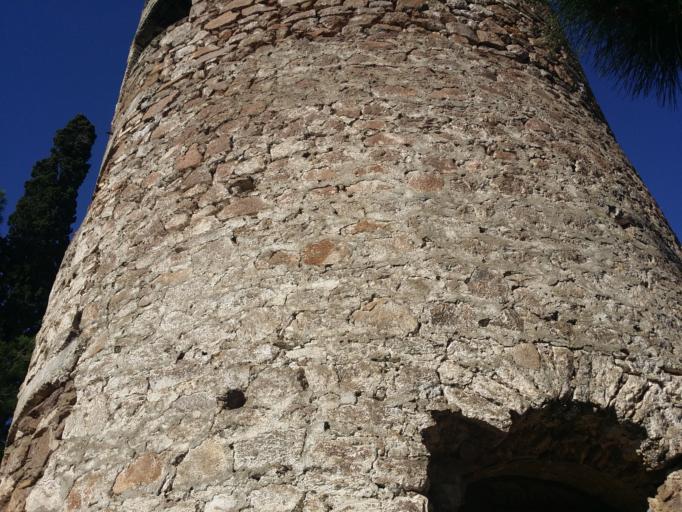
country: GR
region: Attica
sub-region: Nomos Piraios
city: Poros
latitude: 37.4998
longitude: 23.4581
